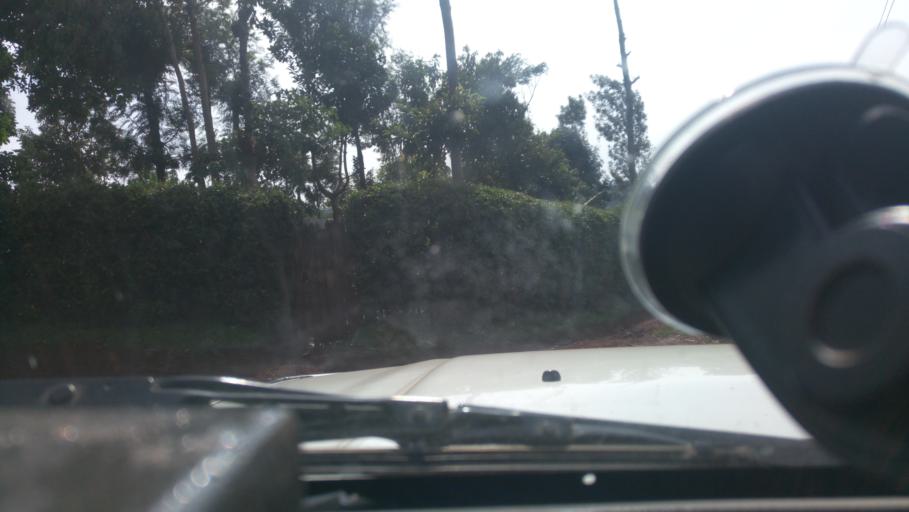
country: KE
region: Nyamira District
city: Nyamira
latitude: -0.5635
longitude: 34.9428
